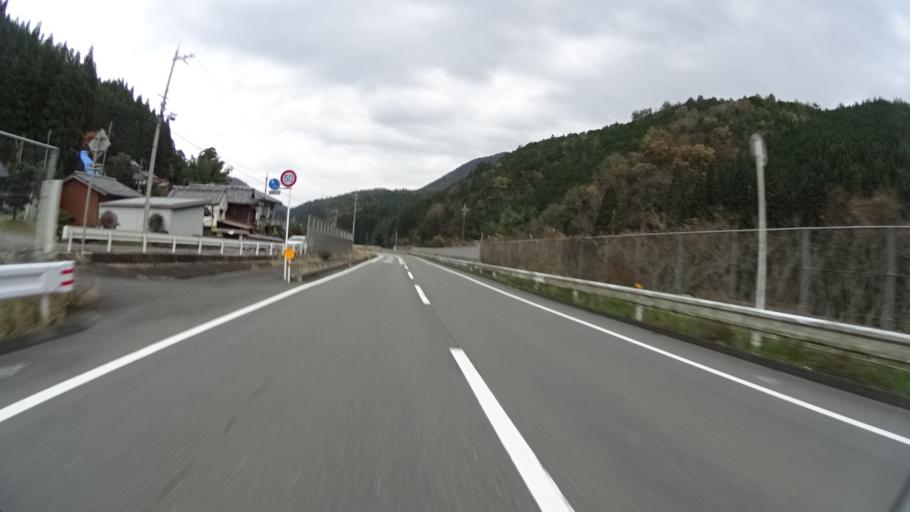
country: JP
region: Hyogo
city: Sasayama
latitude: 35.0675
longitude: 135.3943
